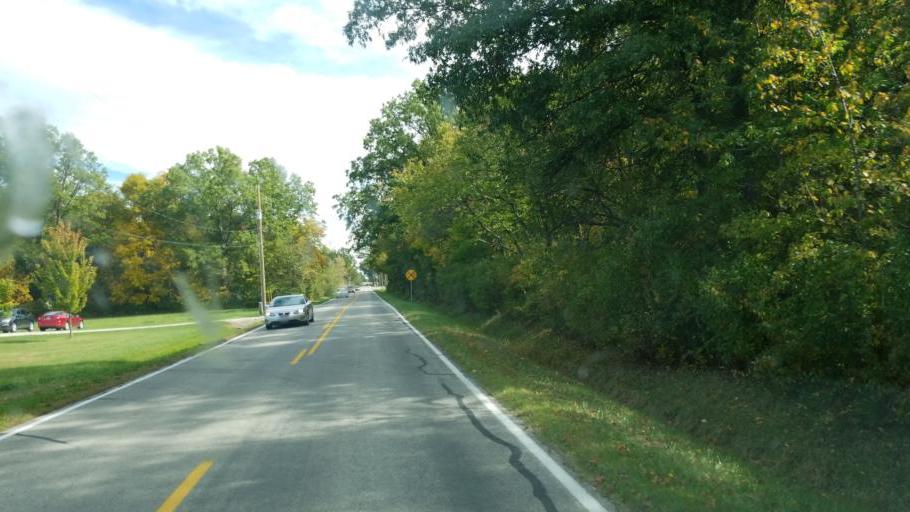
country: US
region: Ohio
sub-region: Erie County
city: Huron
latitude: 41.3647
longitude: -82.4648
